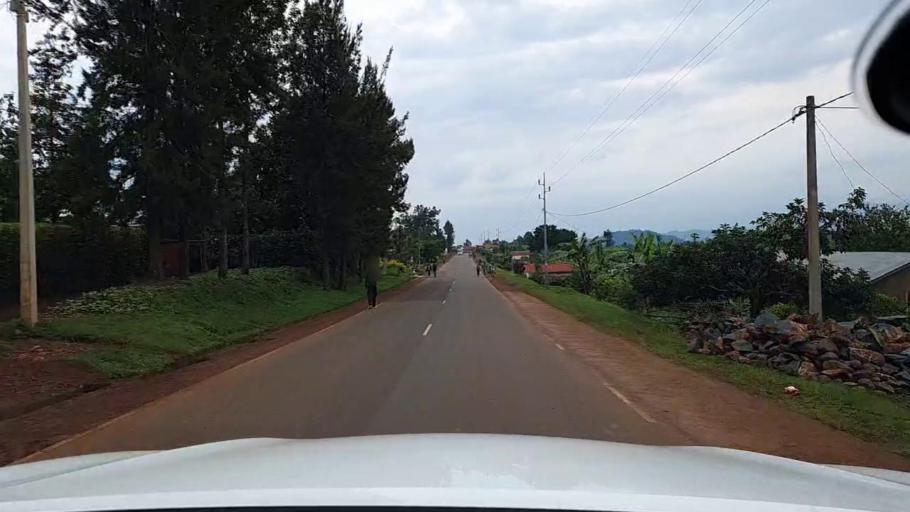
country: RW
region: Western Province
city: Cyangugu
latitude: -2.6403
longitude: 28.9529
